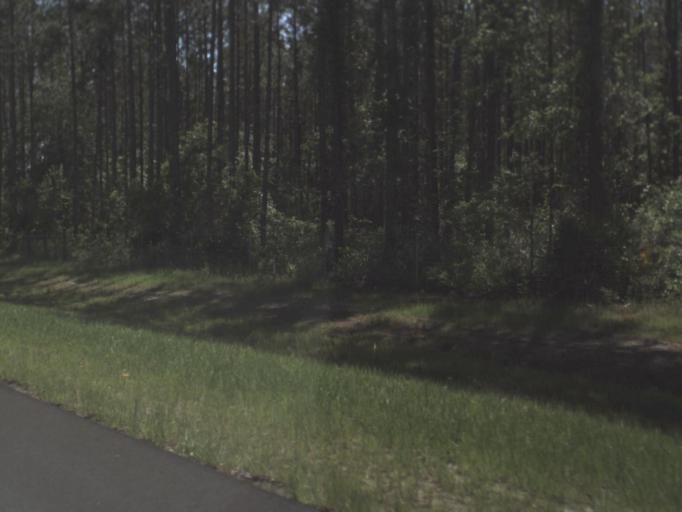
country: US
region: Florida
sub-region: Duval County
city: Baldwin
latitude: 30.3390
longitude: -81.9557
